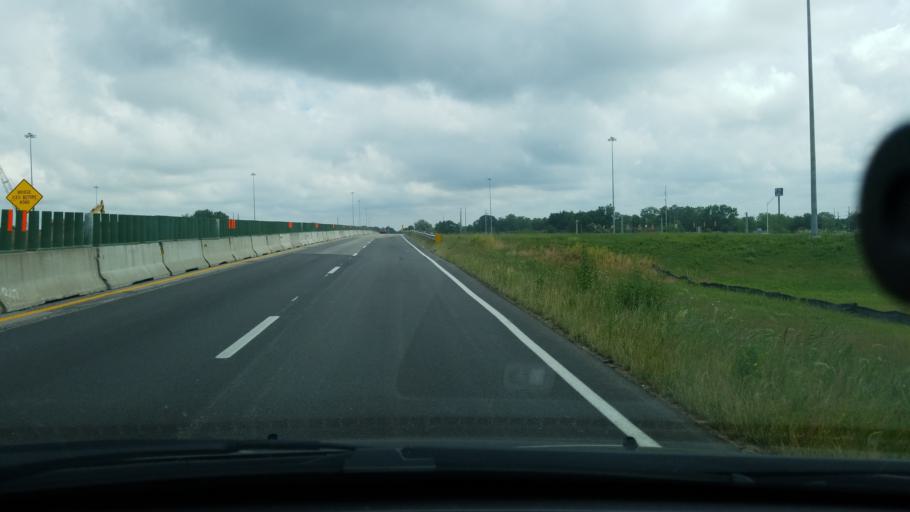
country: US
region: Ohio
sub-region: Lorain County
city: Sheffield
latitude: 41.4043
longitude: -82.1196
